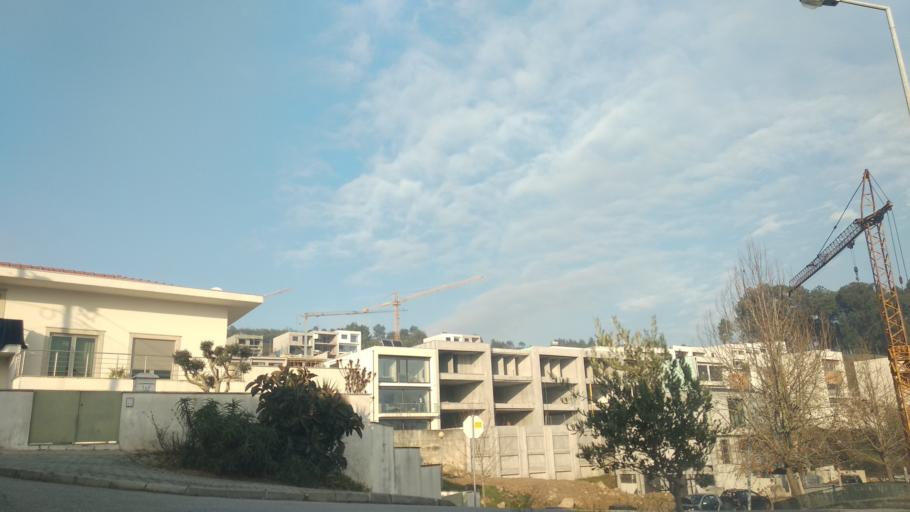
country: PT
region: Braga
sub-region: Braga
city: Adaufe
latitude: 41.5714
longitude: -8.3787
